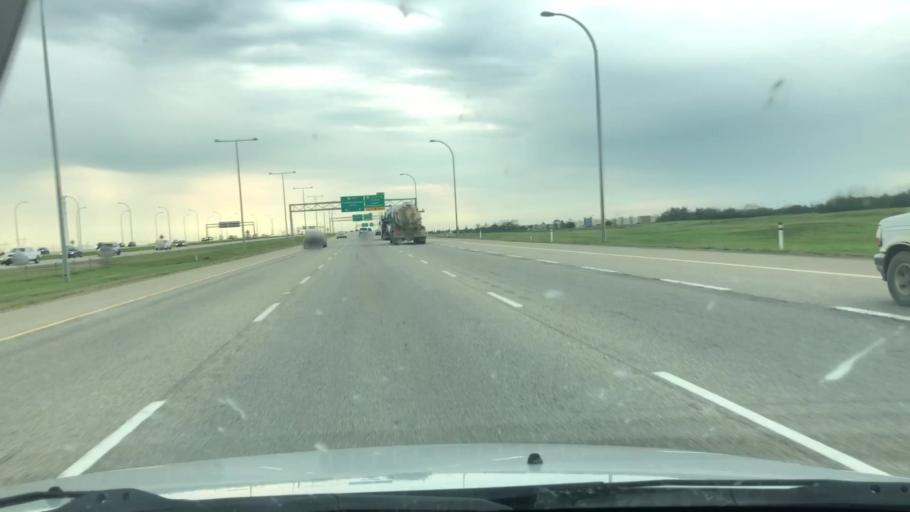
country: CA
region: Alberta
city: Beaumont
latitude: 53.4377
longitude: -113.4711
